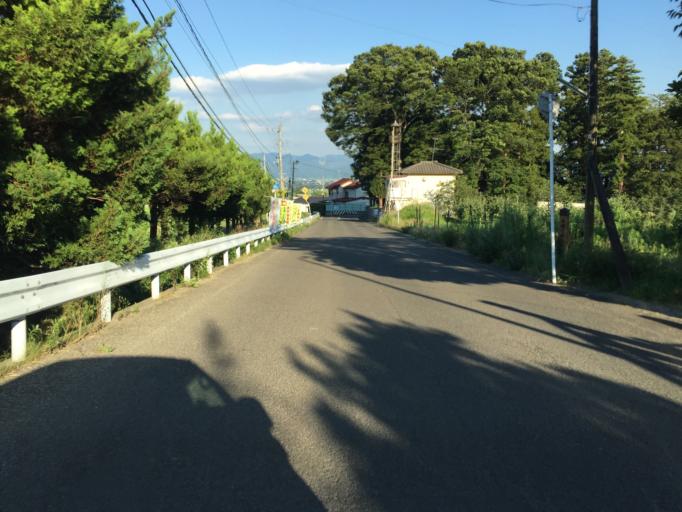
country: JP
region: Fukushima
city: Hobaramachi
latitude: 37.8743
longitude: 140.5203
